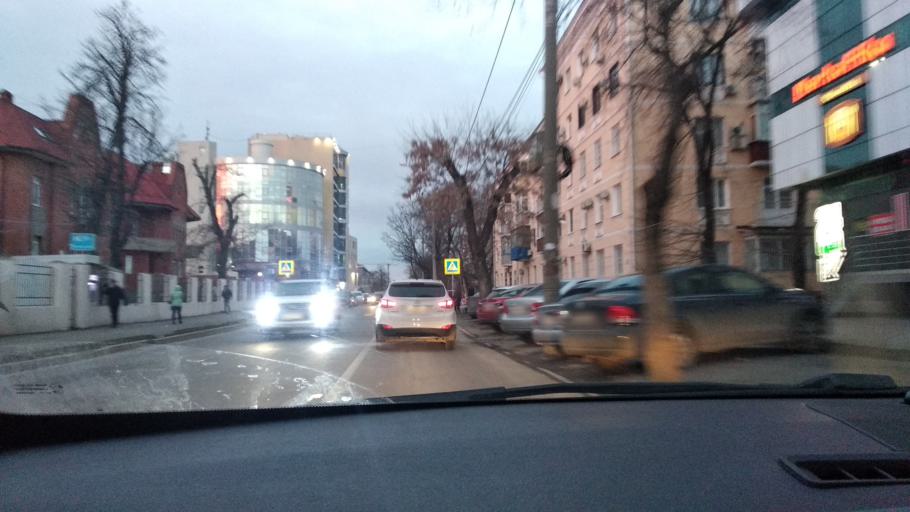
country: RU
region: Krasnodarskiy
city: Krasnodar
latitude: 45.0440
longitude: 38.9748
